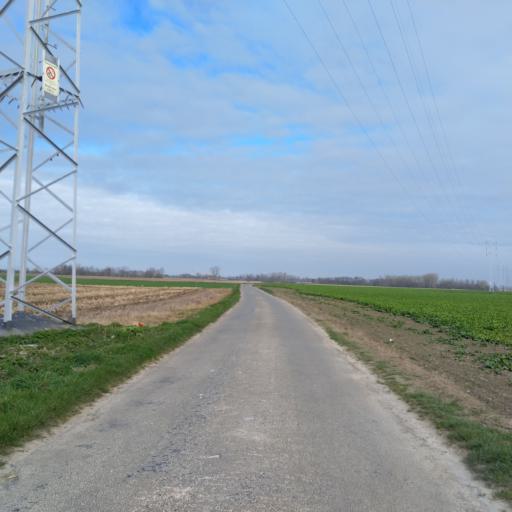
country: BE
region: Wallonia
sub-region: Province du Hainaut
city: Lens
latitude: 50.5687
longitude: 3.9025
